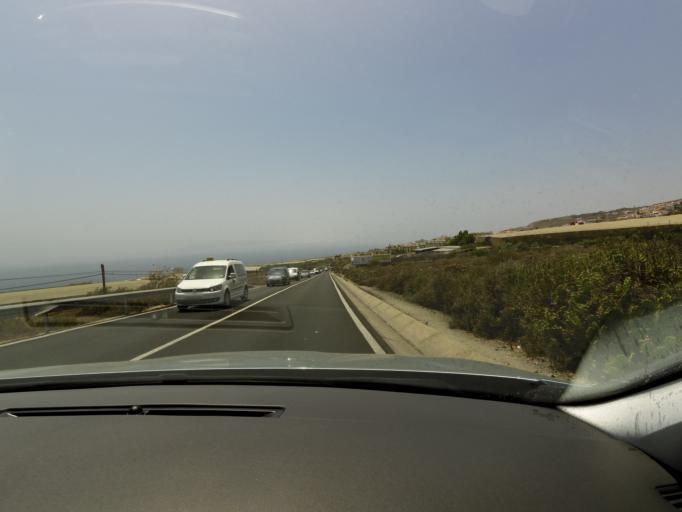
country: ES
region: Canary Islands
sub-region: Provincia de Santa Cruz de Tenerife
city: Adeje
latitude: 28.1262
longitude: -16.7492
